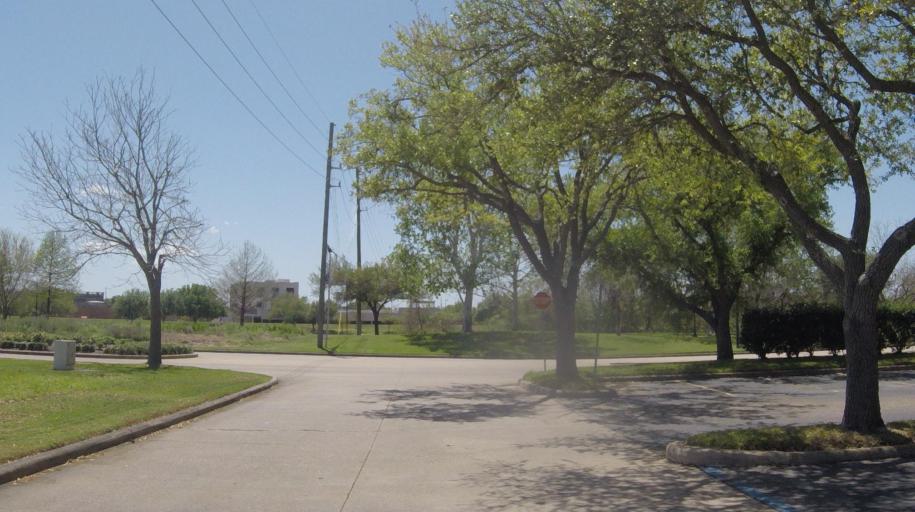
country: US
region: Texas
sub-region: Fort Bend County
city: Sugar Land
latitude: 29.6035
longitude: -95.6274
